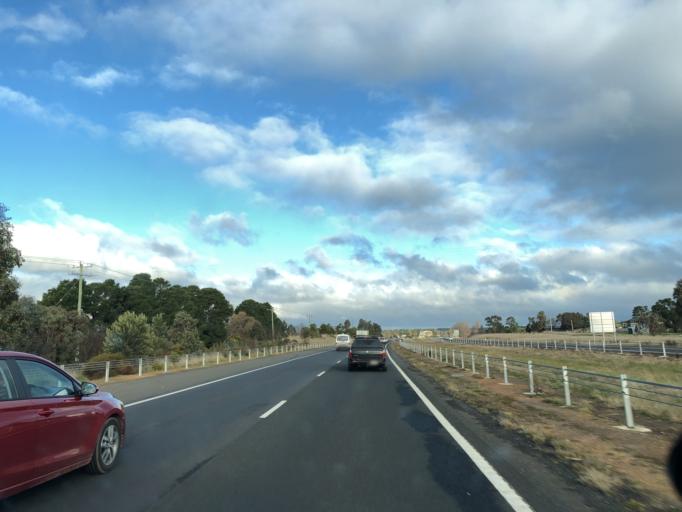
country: AU
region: Victoria
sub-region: Mount Alexander
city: Castlemaine
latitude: -37.2068
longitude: 144.4104
